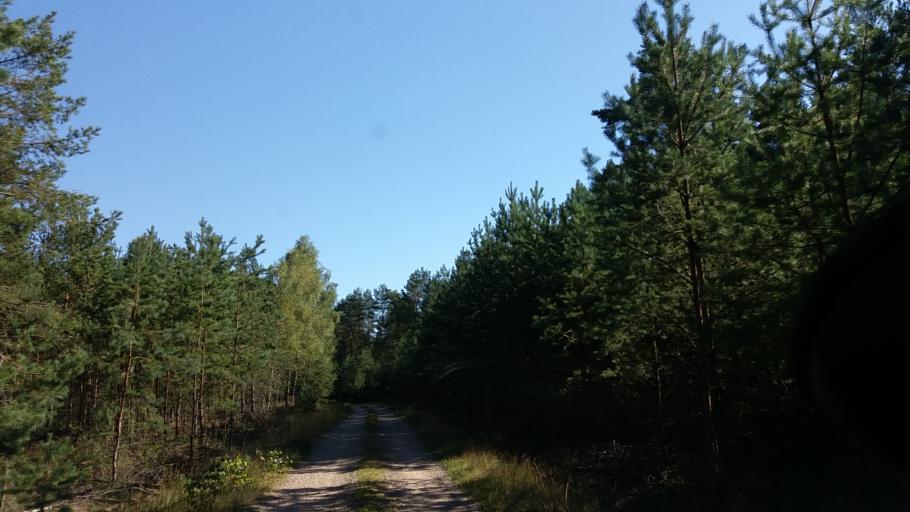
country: PL
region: West Pomeranian Voivodeship
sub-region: Powiat szczecinecki
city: Borne Sulinowo
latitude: 53.5574
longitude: 16.5057
